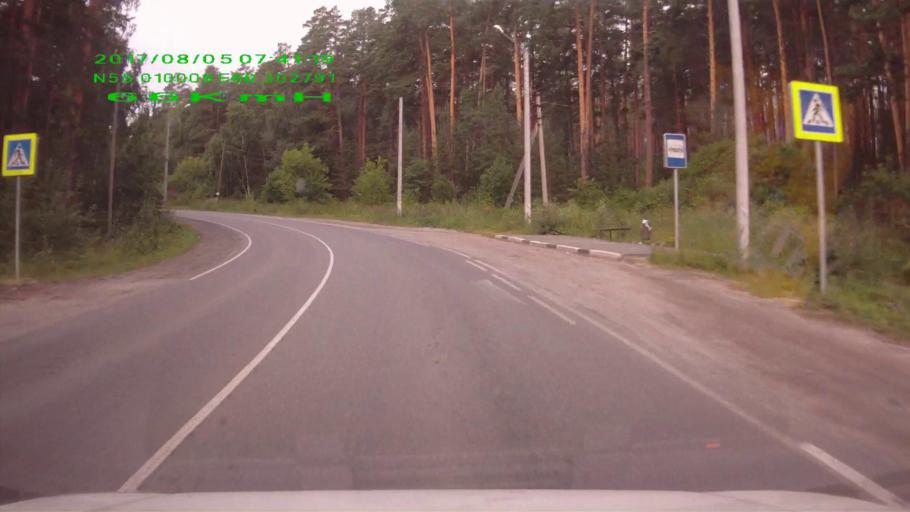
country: RU
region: Chelyabinsk
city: Chebarkul'
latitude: 55.0099
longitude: 60.3024
